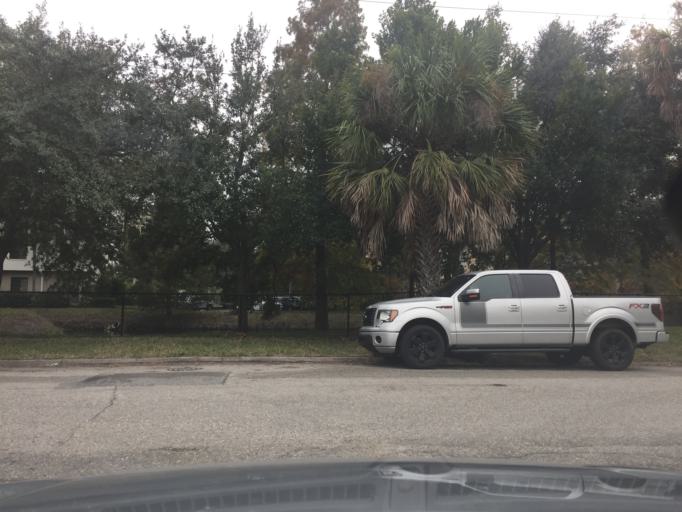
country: US
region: Florida
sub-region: Hillsborough County
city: Tampa
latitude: 27.9402
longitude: -82.4865
